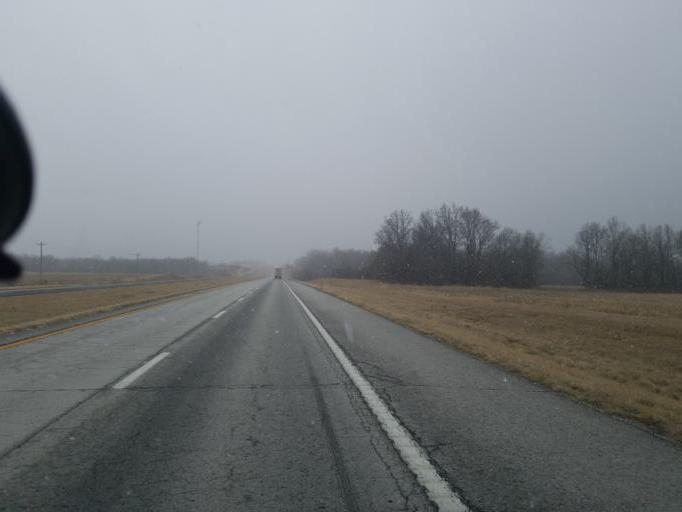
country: US
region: Missouri
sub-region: Macon County
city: La Plata
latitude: 39.9271
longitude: -92.4758
